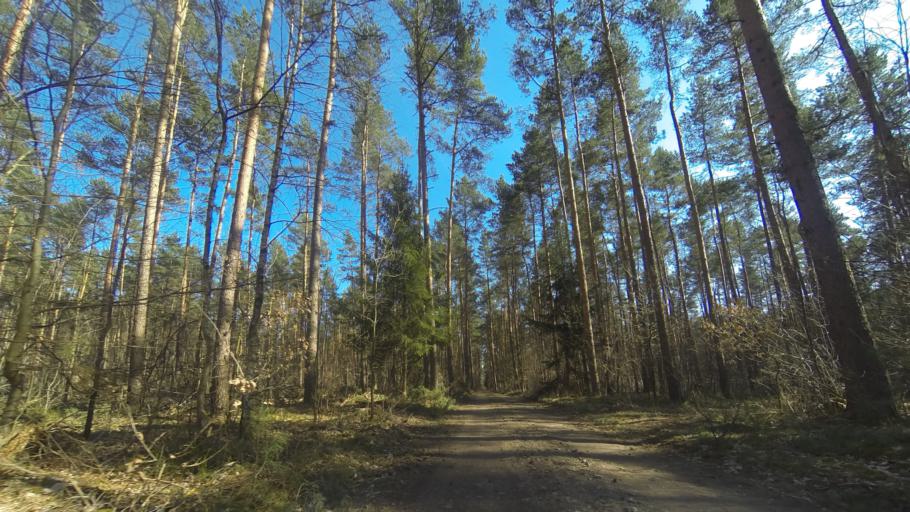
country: DE
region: Saxony
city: Laussnitz
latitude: 51.2636
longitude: 13.8500
